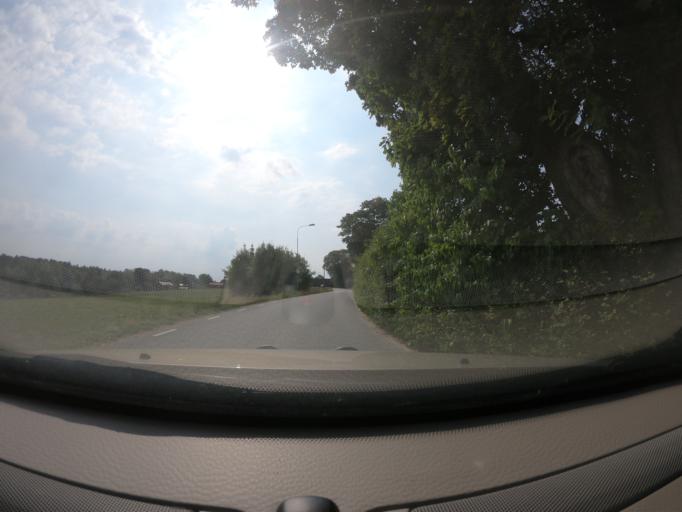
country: SE
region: Joenkoeping
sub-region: Vetlanda Kommun
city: Landsbro
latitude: 57.2933
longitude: 14.8792
